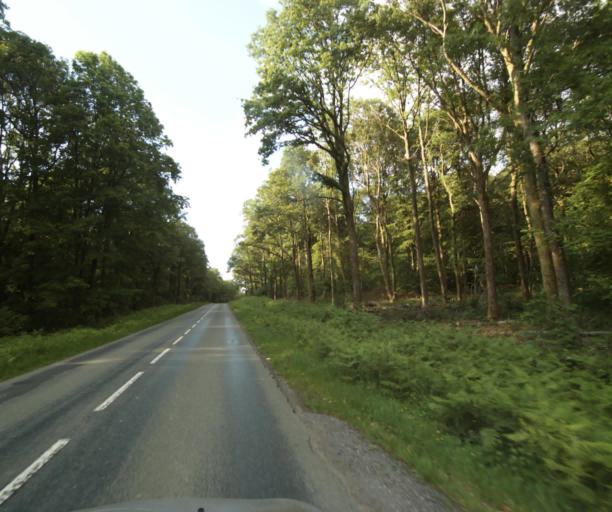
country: FR
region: Champagne-Ardenne
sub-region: Departement des Ardennes
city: Nouzonville
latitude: 49.8226
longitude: 4.6981
